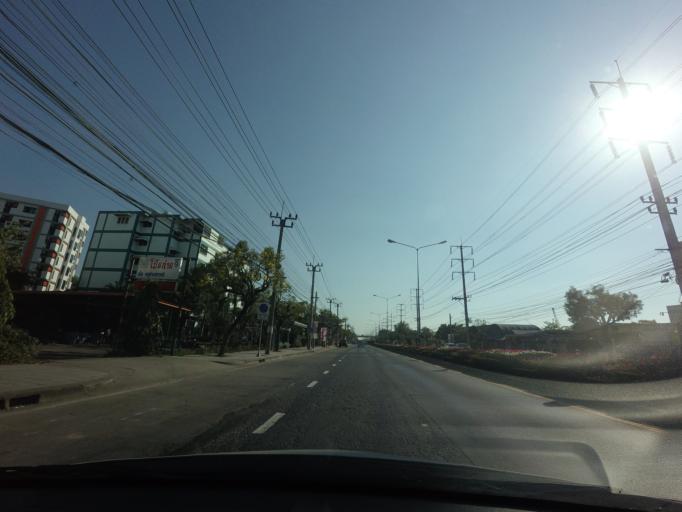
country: TH
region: Bangkok
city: Nong Chok
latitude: 13.8446
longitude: 100.8573
